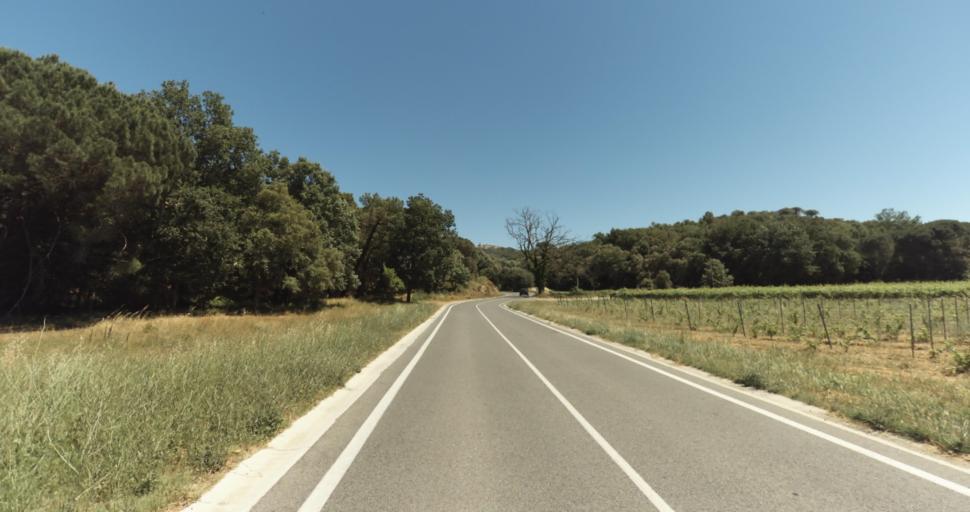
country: FR
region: Provence-Alpes-Cote d'Azur
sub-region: Departement du Var
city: Gassin
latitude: 43.2387
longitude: 6.5687
